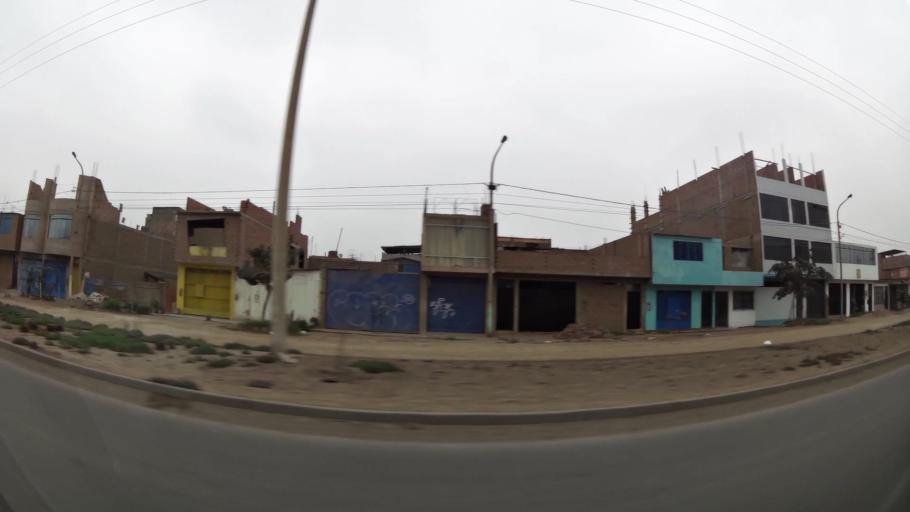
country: PE
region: Lima
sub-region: Lima
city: Urb. Santo Domingo
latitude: -11.8802
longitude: -77.0278
